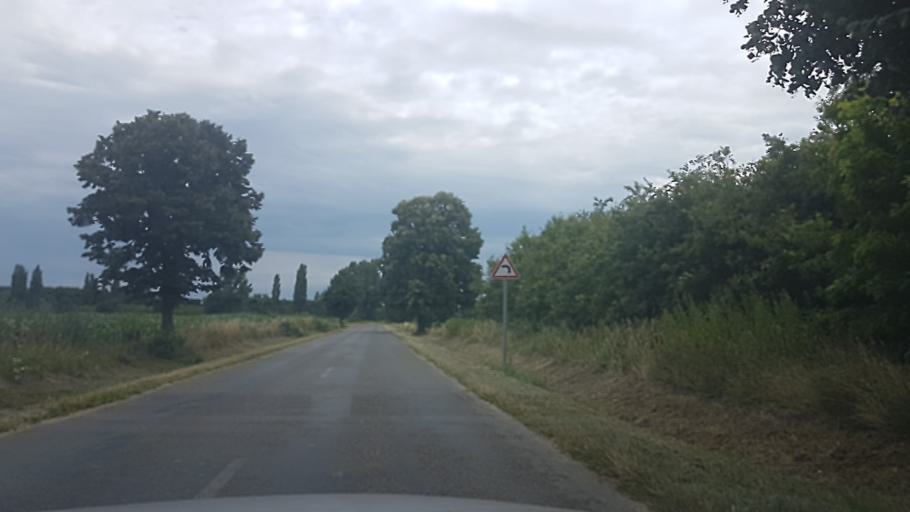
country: HU
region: Somogy
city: Barcs
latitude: 45.9563
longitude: 17.5986
